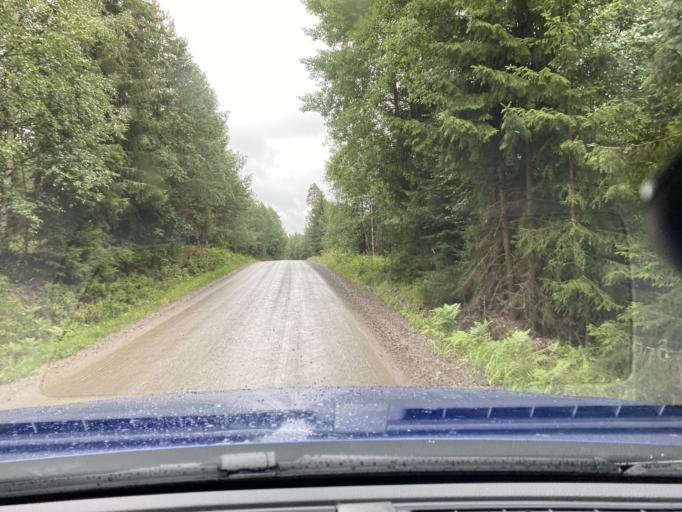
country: FI
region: Pirkanmaa
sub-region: Lounais-Pirkanmaa
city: Punkalaidun
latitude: 61.1486
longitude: 23.2552
